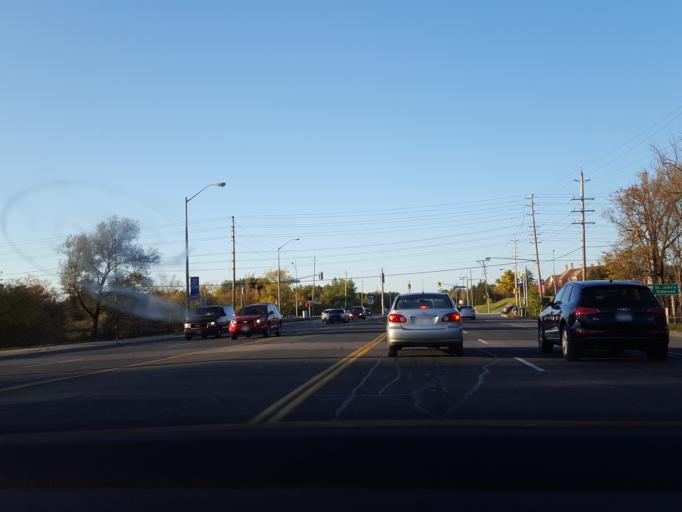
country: CA
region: Ontario
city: Newmarket
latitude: 44.0169
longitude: -79.4716
